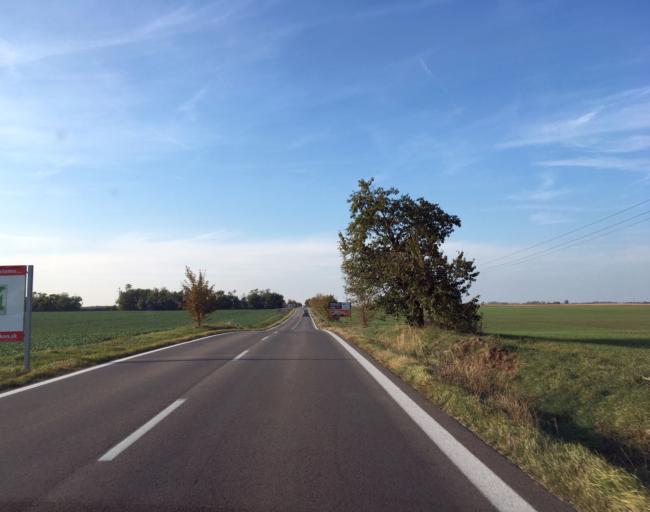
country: SK
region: Nitriansky
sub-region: Okres Nove Zamky
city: Nove Zamky
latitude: 48.0230
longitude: 18.1420
